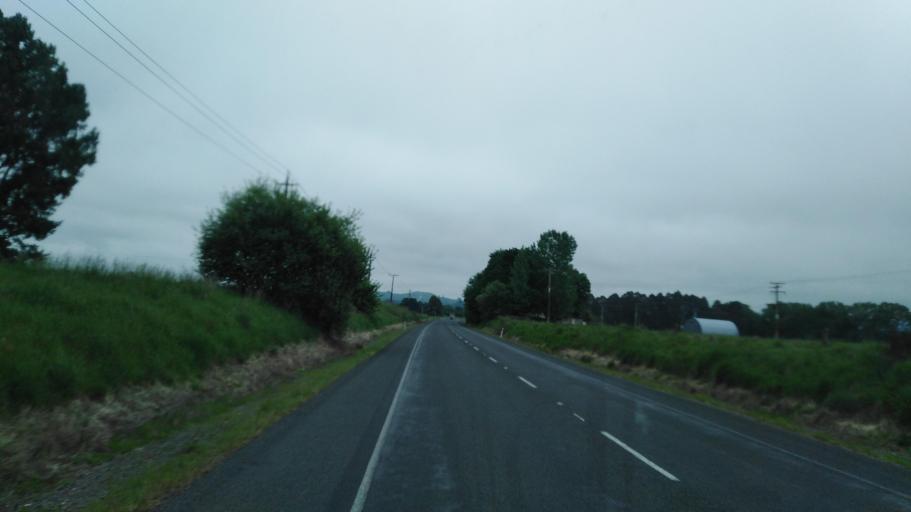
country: NZ
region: Bay of Plenty
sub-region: Rotorua District
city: Rotorua
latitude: -38.3935
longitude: 176.3375
